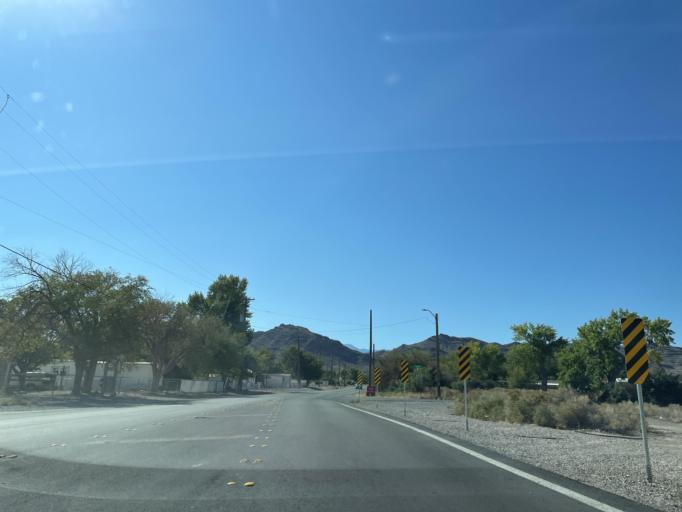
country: US
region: Nevada
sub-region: Nye County
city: Pahrump
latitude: 36.5767
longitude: -115.6699
